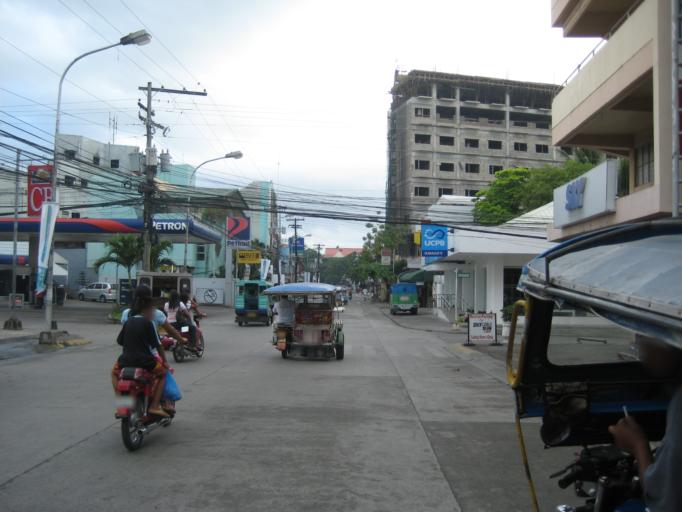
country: PH
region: Central Visayas
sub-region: Province of Negros Oriental
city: Dumaguete
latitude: 9.3079
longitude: 123.3056
